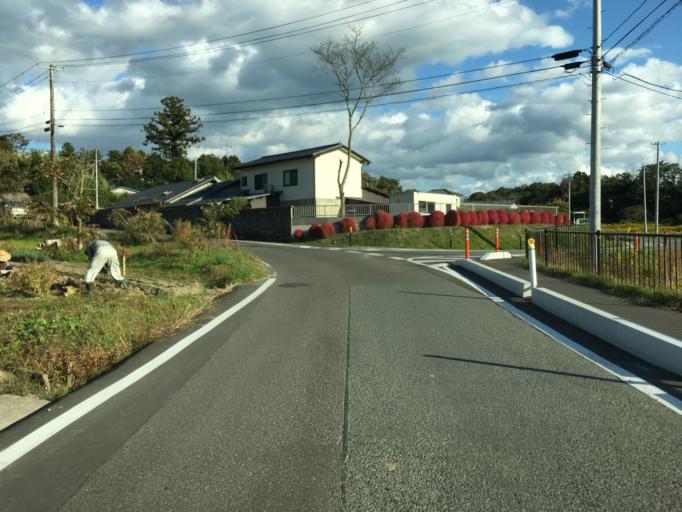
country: JP
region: Miyagi
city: Marumori
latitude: 37.8690
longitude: 140.9321
